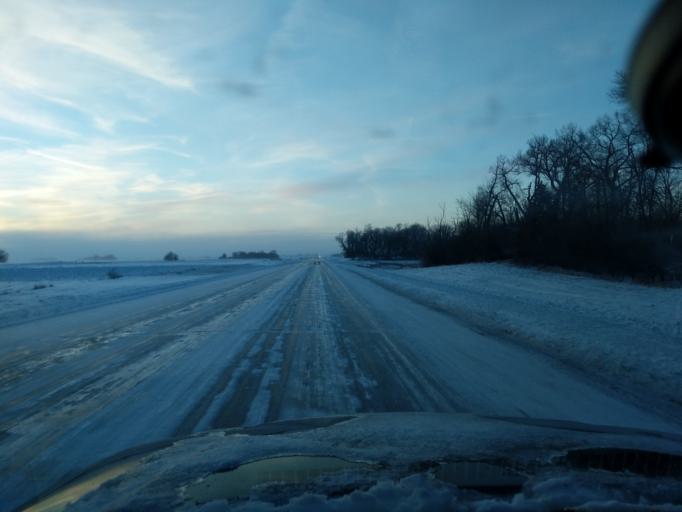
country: US
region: Minnesota
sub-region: Renville County
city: Renville
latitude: 44.7891
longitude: -95.2882
